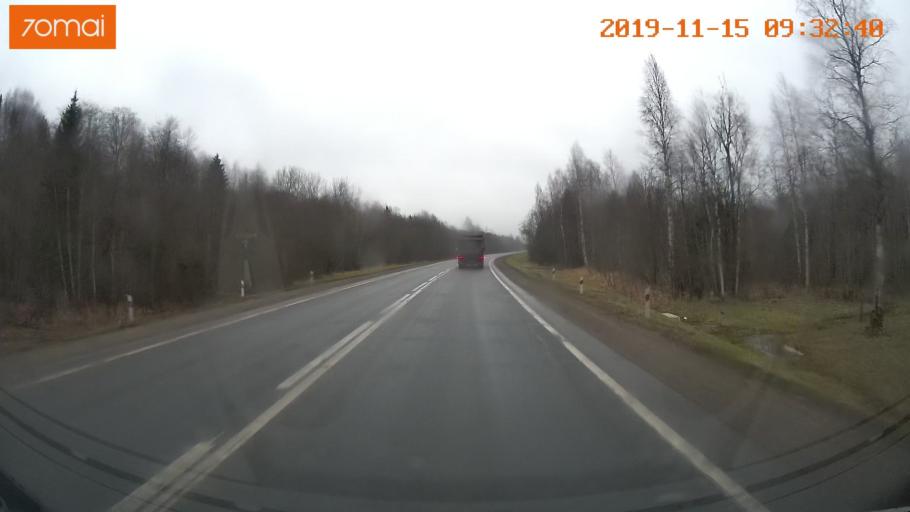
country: RU
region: Vologda
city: Sheksna
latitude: 59.2706
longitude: 38.3407
